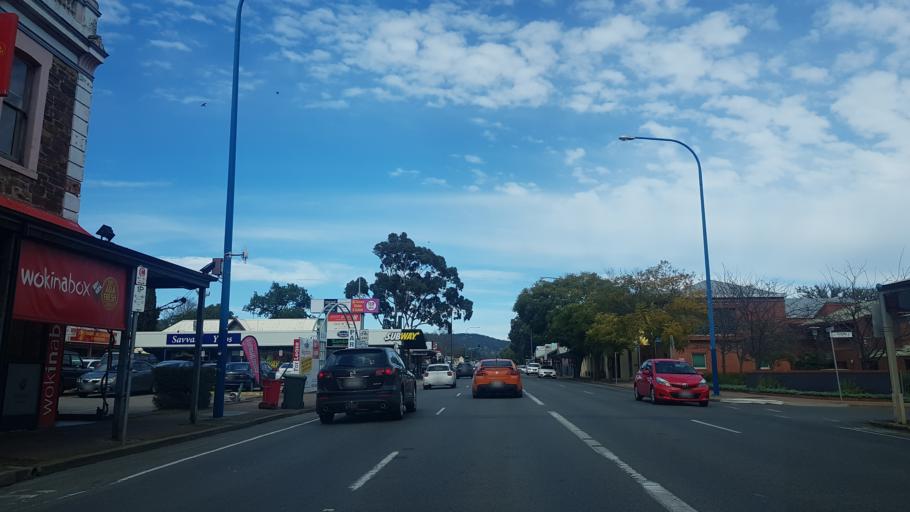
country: AU
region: South Australia
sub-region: Unley
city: Unley Park
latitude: -34.9568
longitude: 138.6080
